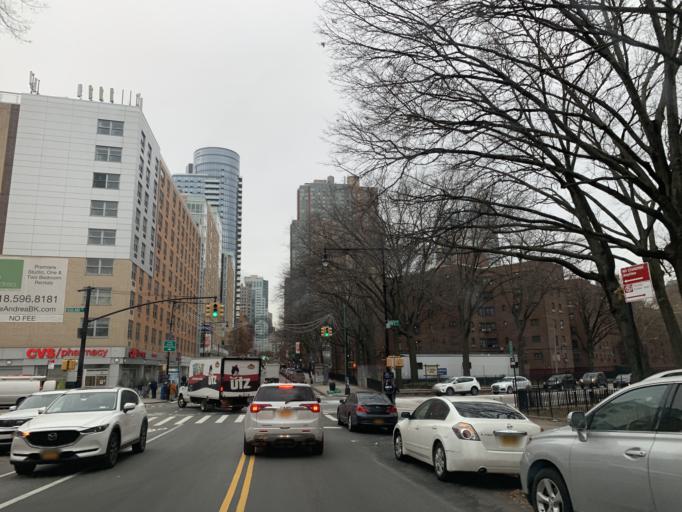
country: US
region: New York
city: New York City
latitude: 40.6935
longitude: -73.9786
